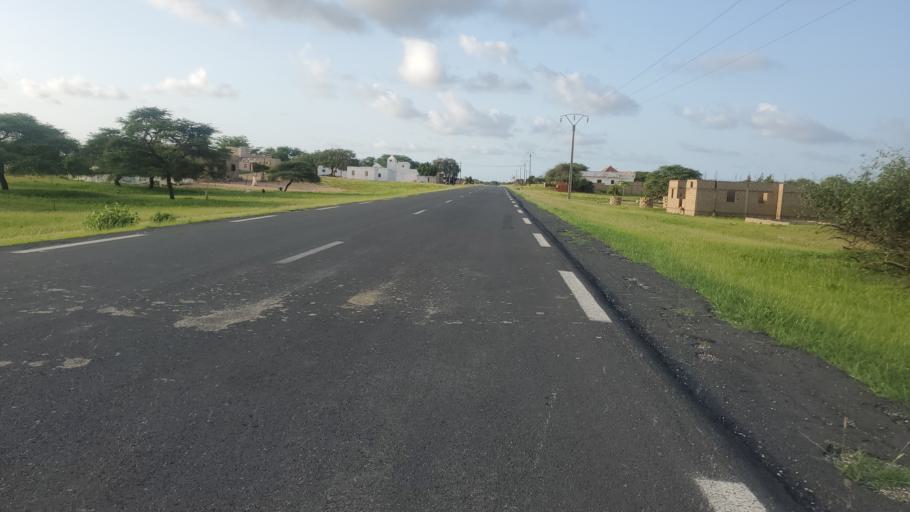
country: SN
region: Saint-Louis
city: Saint-Louis
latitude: 16.1514
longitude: -16.4097
